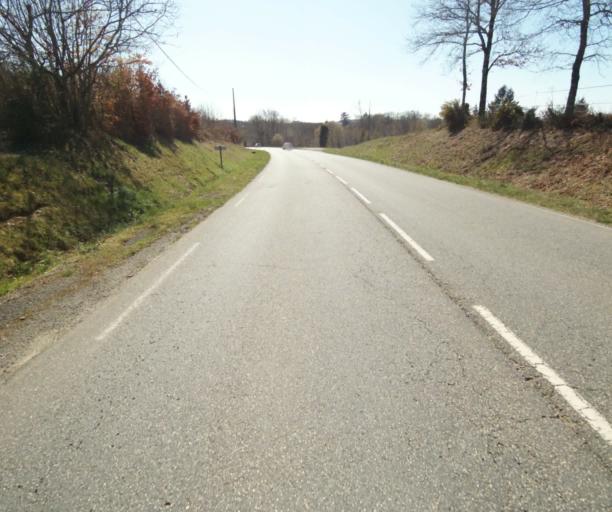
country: FR
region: Limousin
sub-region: Departement de la Correze
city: Saint-Mexant
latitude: 45.3007
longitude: 1.6732
